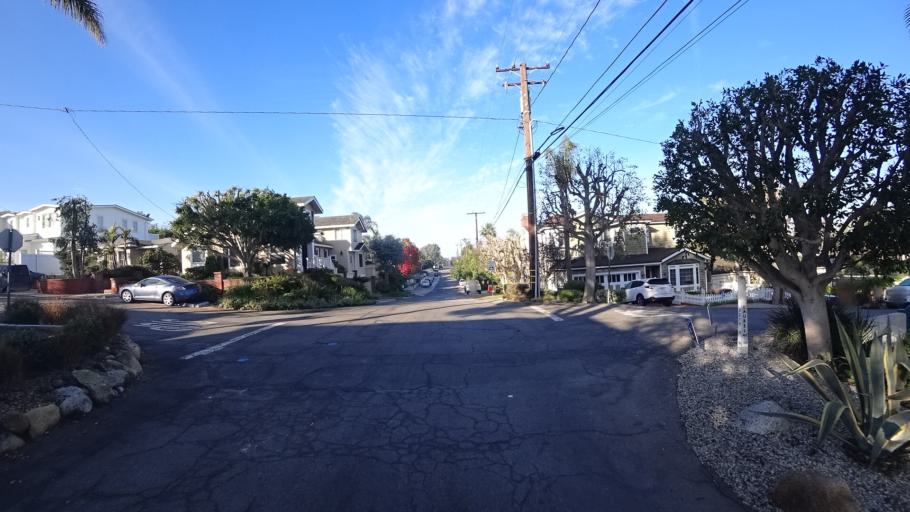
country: US
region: California
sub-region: Los Angeles County
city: Manhattan Beach
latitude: 33.9000
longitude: -118.4042
